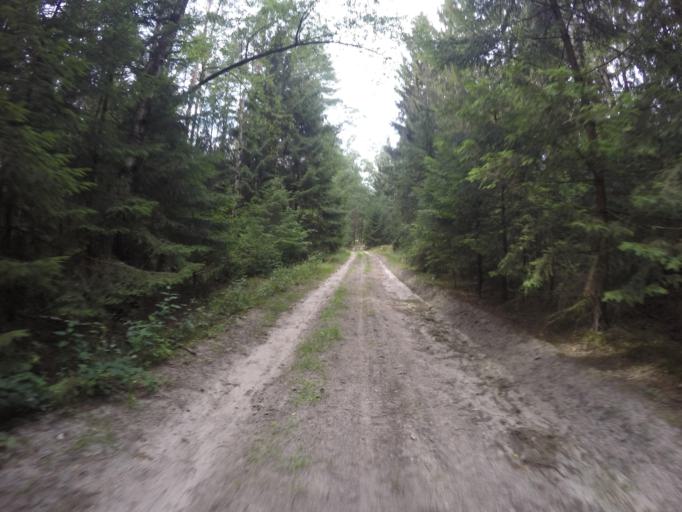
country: DE
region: Lower Saxony
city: Thomasburg
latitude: 53.2385
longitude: 10.6888
